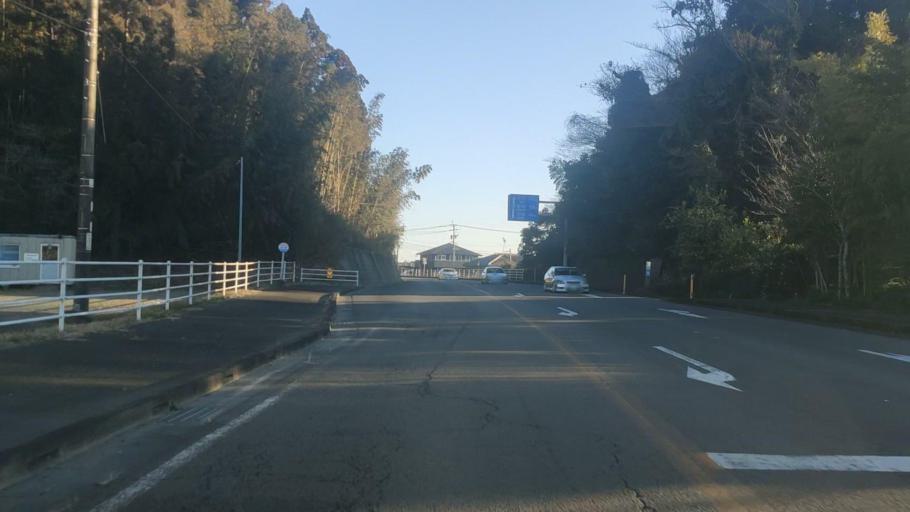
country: JP
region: Miyazaki
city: Takanabe
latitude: 32.0782
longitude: 131.5073
